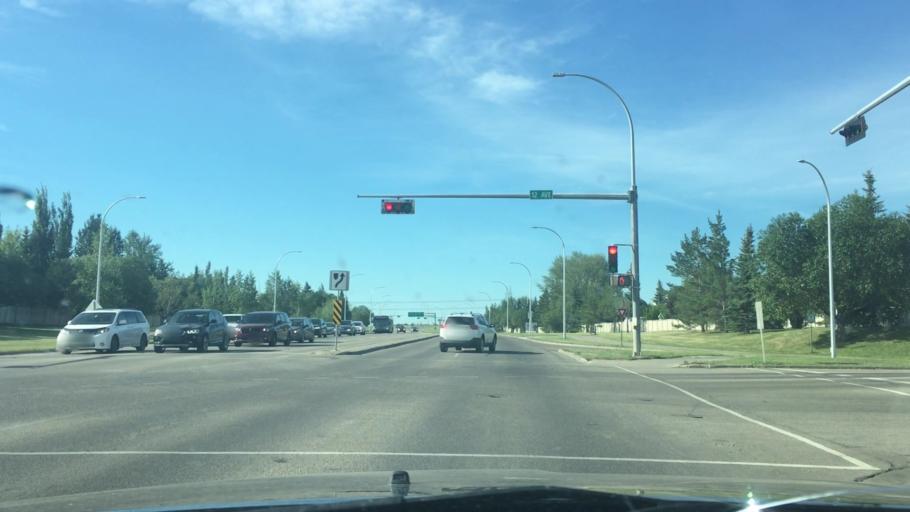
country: CA
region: Alberta
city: Edmonton
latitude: 53.4429
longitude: -113.5179
